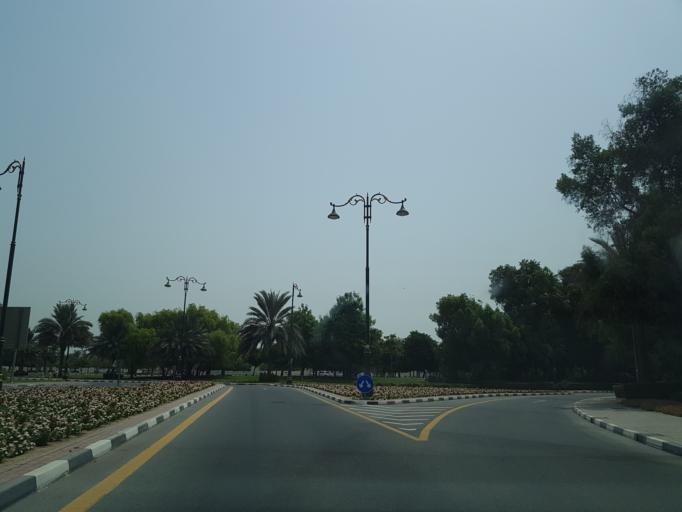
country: AE
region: Ash Shariqah
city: Sharjah
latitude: 25.2277
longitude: 55.3003
